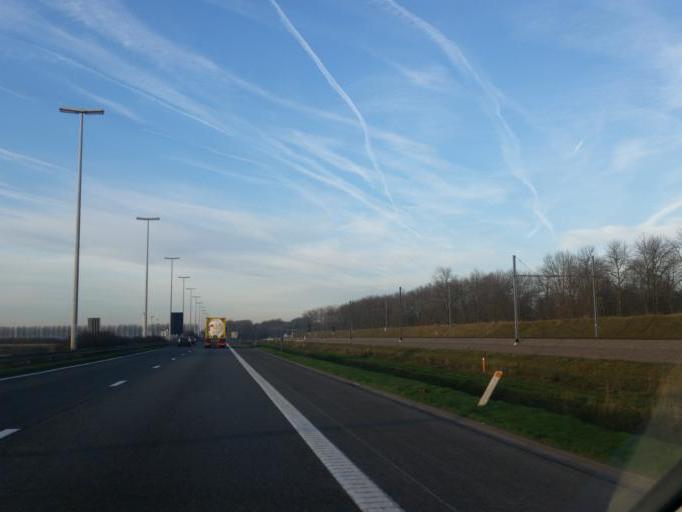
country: BE
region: Flanders
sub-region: Provincie Oost-Vlaanderen
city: Beveren
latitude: 51.2422
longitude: 4.2239
